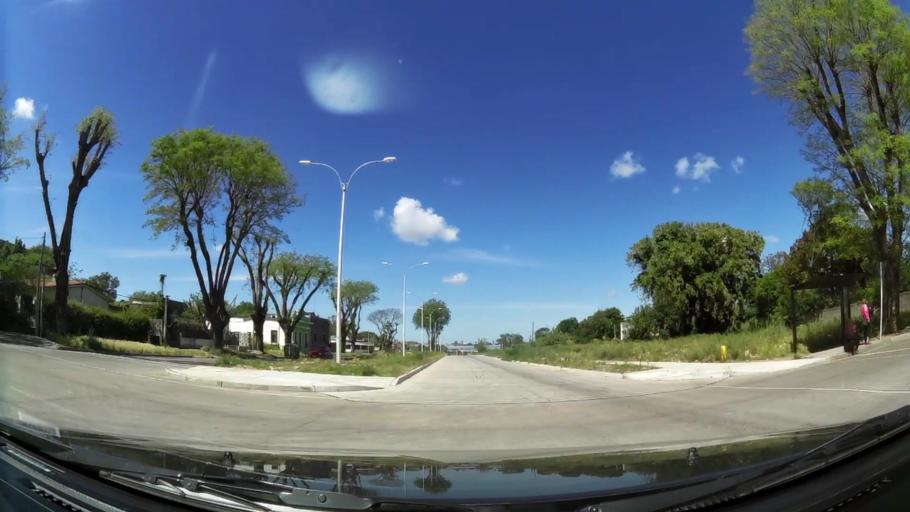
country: UY
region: Montevideo
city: Montevideo
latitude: -34.8461
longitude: -56.1456
